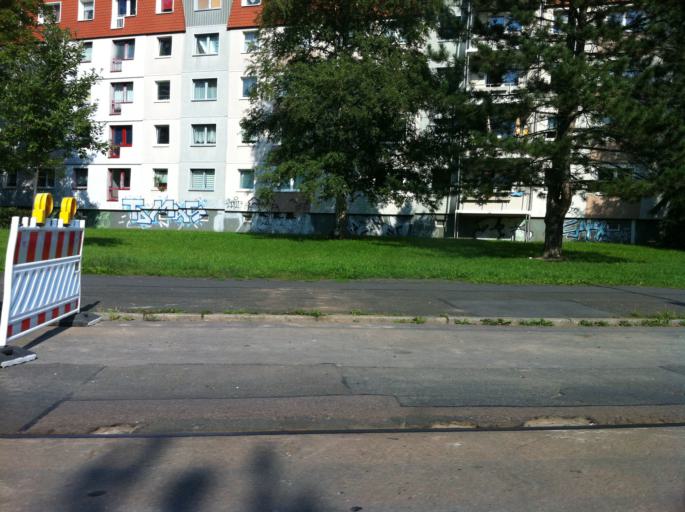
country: DE
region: Saxony
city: Markkleeberg
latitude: 51.2945
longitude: 12.3867
